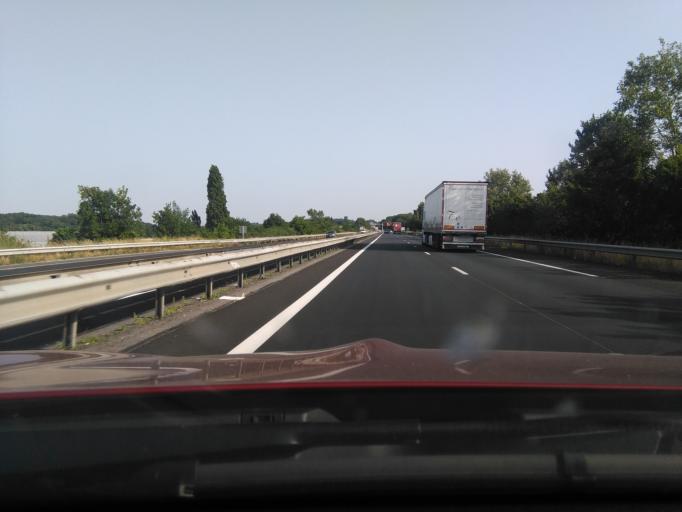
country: FR
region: Rhone-Alpes
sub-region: Departement du Rhone
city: Sathonay-Village
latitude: 45.8495
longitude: 4.9110
